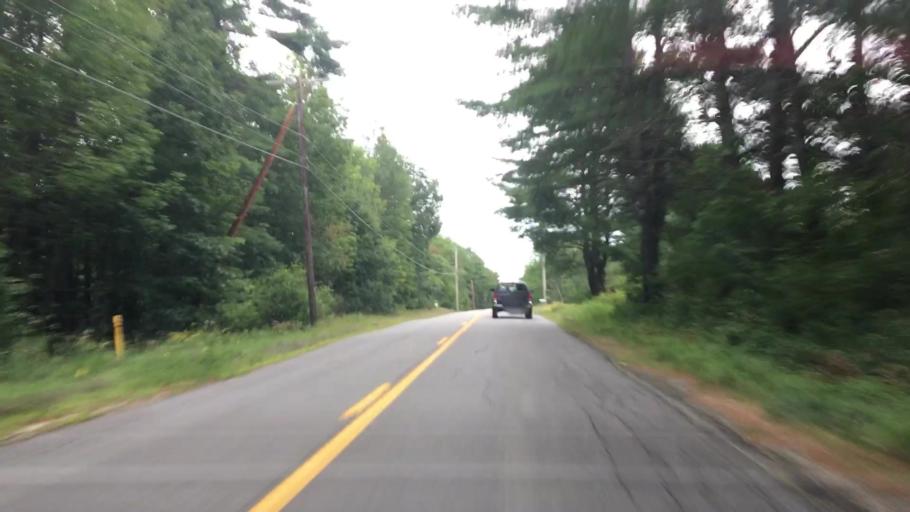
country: US
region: Maine
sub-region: Cumberland County
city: Freeport
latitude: 43.8827
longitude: -70.1648
